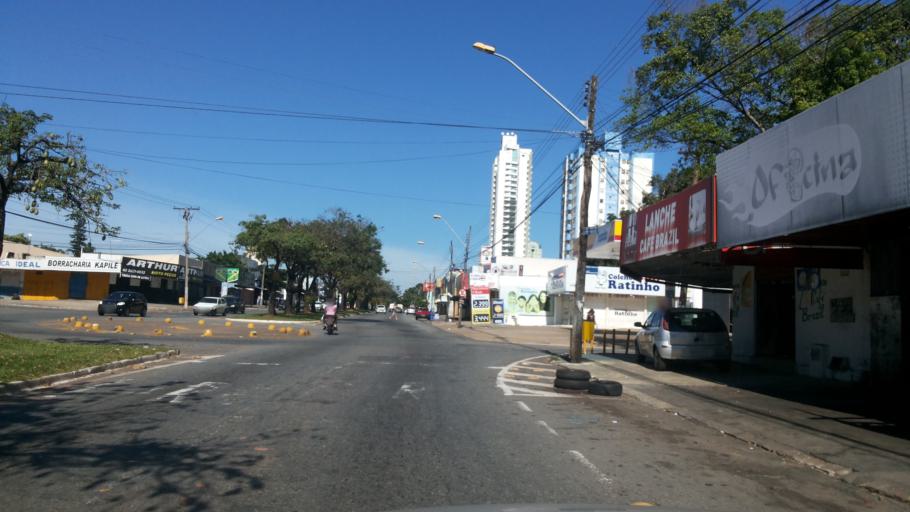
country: BR
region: Goias
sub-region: Goiania
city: Goiania
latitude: -16.7161
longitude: -49.2550
